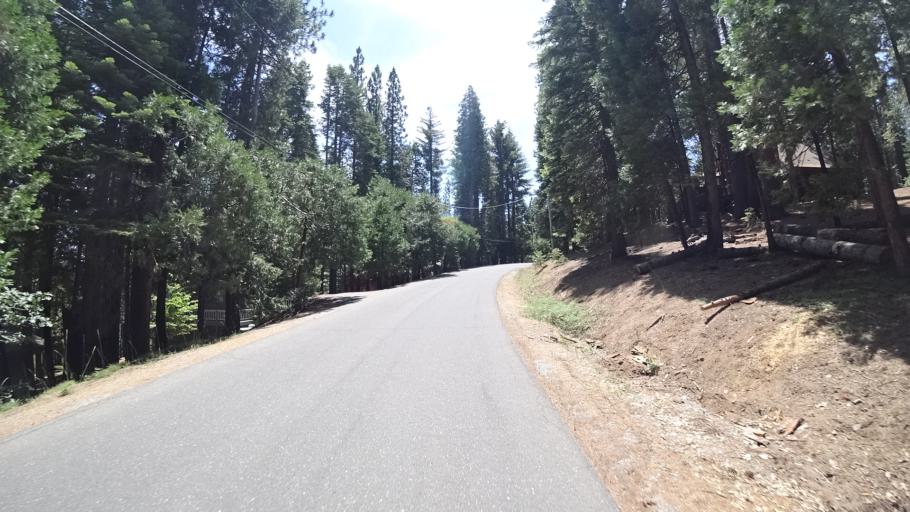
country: US
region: California
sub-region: Calaveras County
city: Arnold
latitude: 38.3034
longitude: -120.2557
